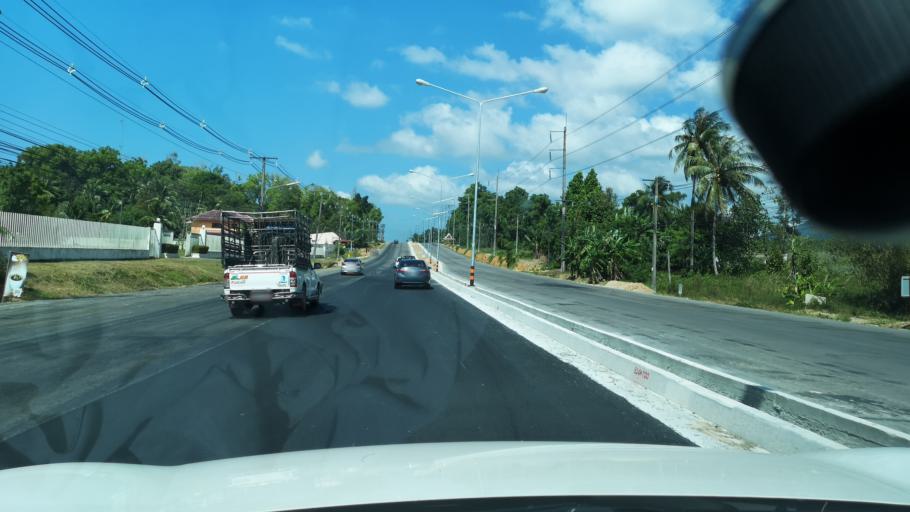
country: TH
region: Phangnga
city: Thai Mueang
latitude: 8.4262
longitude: 98.2585
